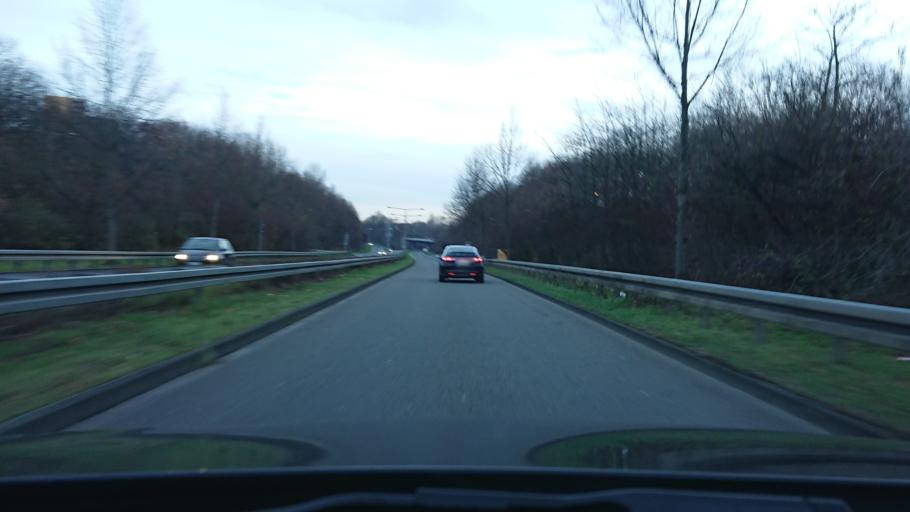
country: DE
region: North Rhine-Westphalia
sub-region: Regierungsbezirk Koln
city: Mengenich
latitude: 51.0238
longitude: 6.8894
